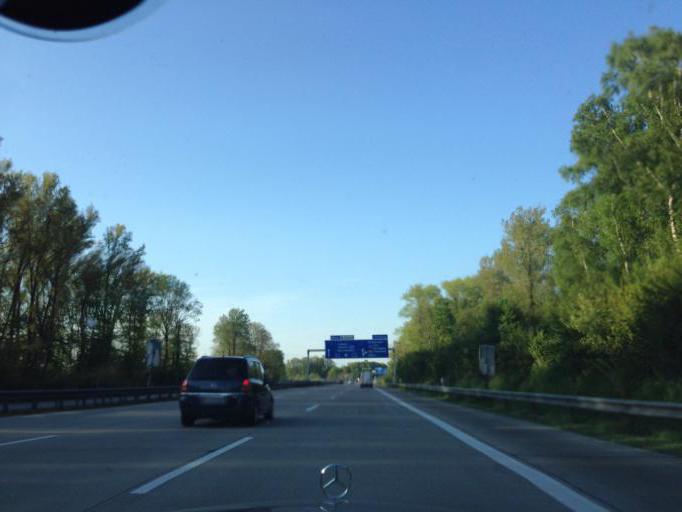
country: DE
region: Schleswig-Holstein
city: Hammoor
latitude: 53.7091
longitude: 10.3319
